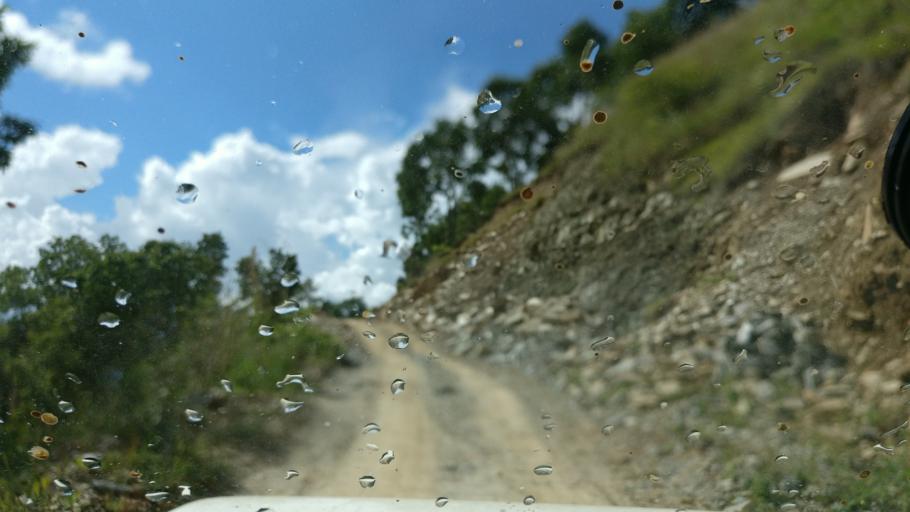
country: NP
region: Western Region
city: Baglung
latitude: 28.2649
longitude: 83.6471
